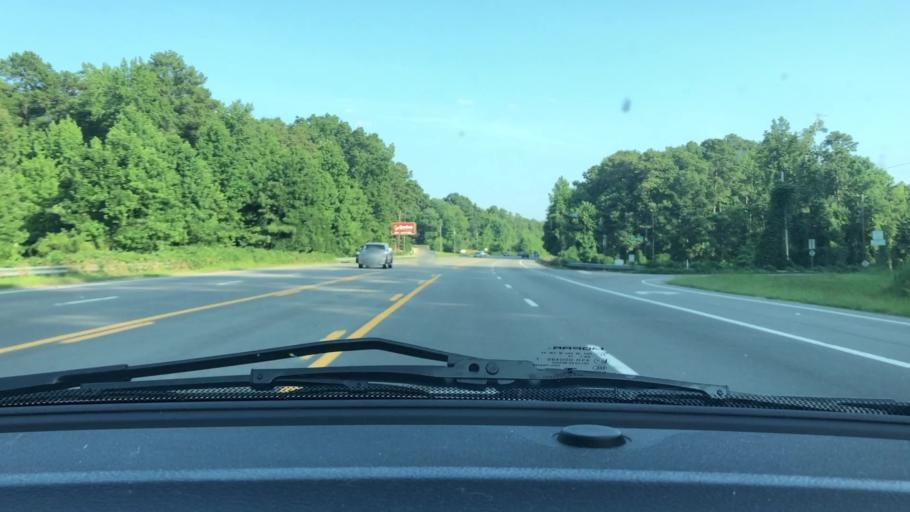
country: US
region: North Carolina
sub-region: Lee County
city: Broadway
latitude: 35.3969
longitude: -79.1104
